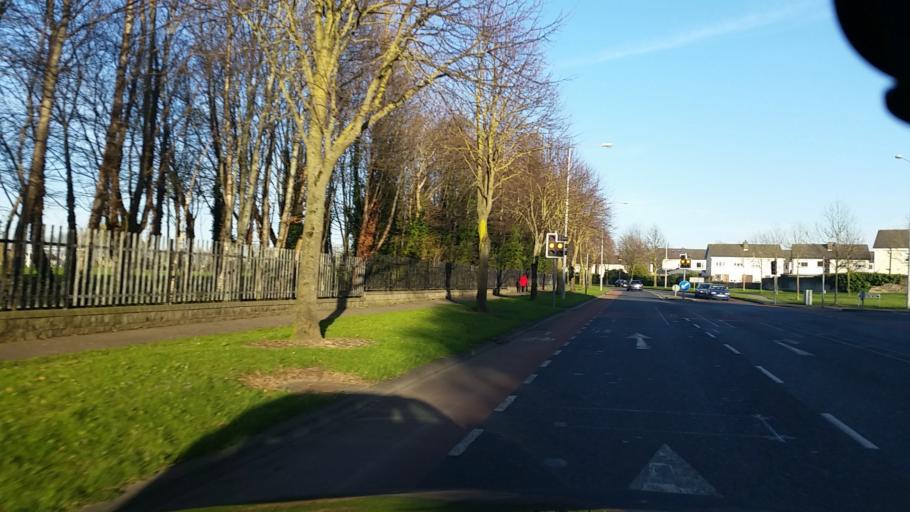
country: IE
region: Leinster
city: Hartstown
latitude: 53.3910
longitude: -6.4139
